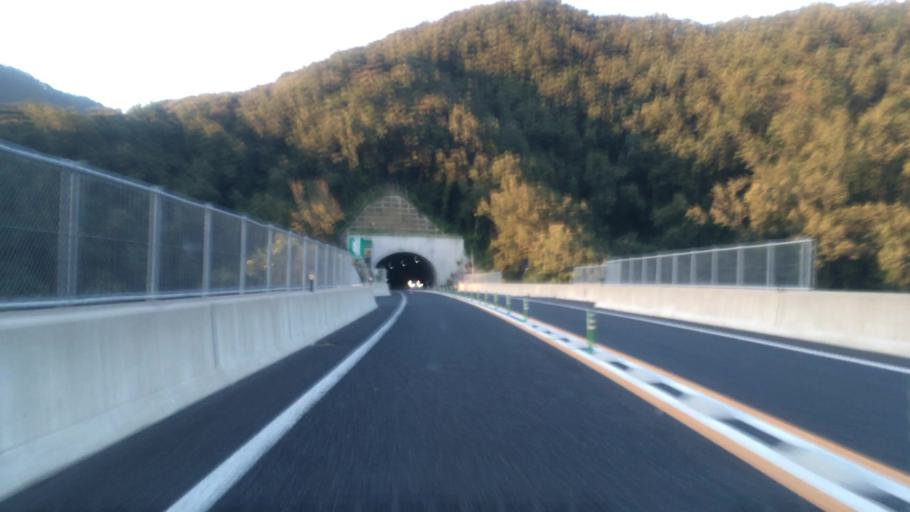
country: JP
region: Tottori
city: Tottori
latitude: 35.5540
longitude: 134.2800
